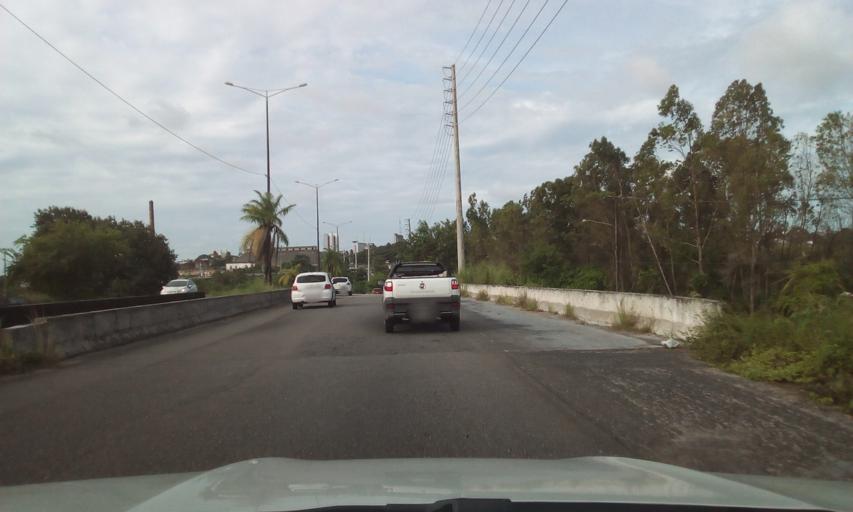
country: BR
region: Paraiba
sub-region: Bayeux
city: Bayeux
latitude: -7.1257
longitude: -34.8969
